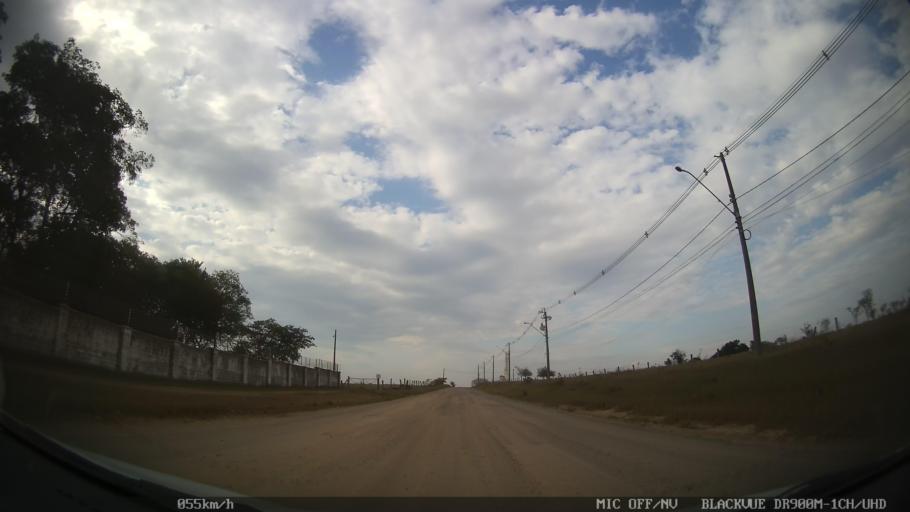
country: BR
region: Sao Paulo
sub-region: Paulinia
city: Paulinia
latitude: -22.7200
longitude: -47.1596
